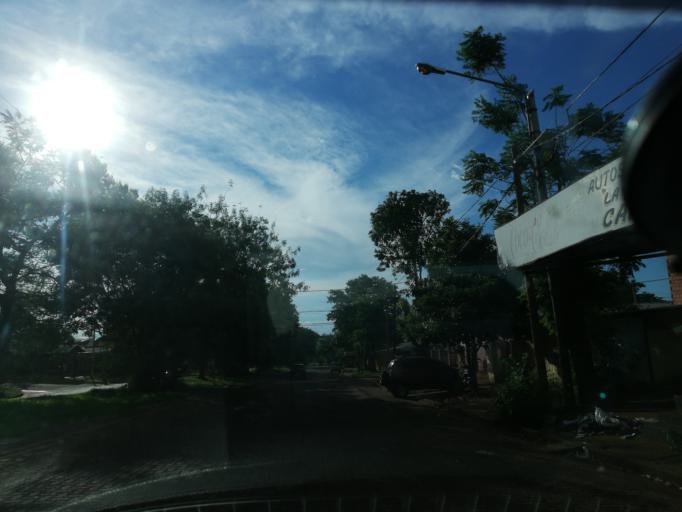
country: AR
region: Misiones
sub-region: Departamento de Capital
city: Posadas
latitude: -27.4153
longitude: -55.9530
